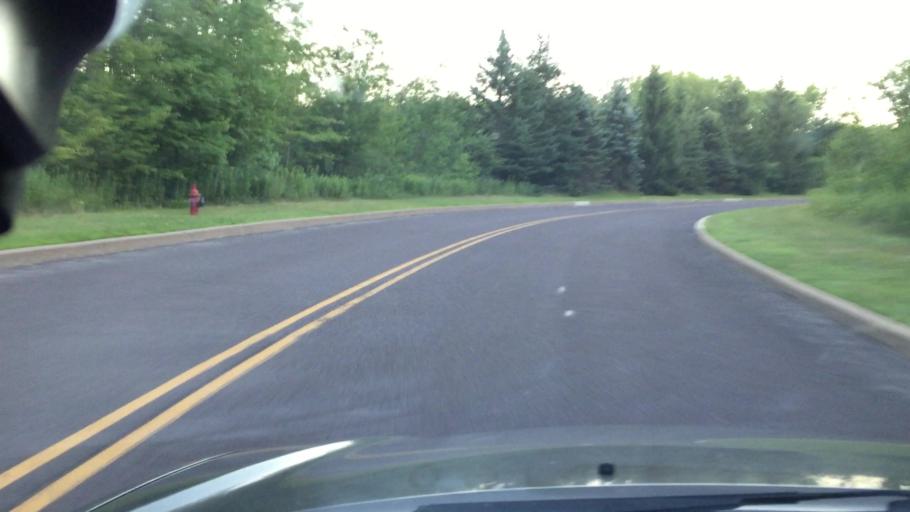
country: US
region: Pennsylvania
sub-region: Luzerne County
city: Harleigh
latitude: 41.0452
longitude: -75.9644
